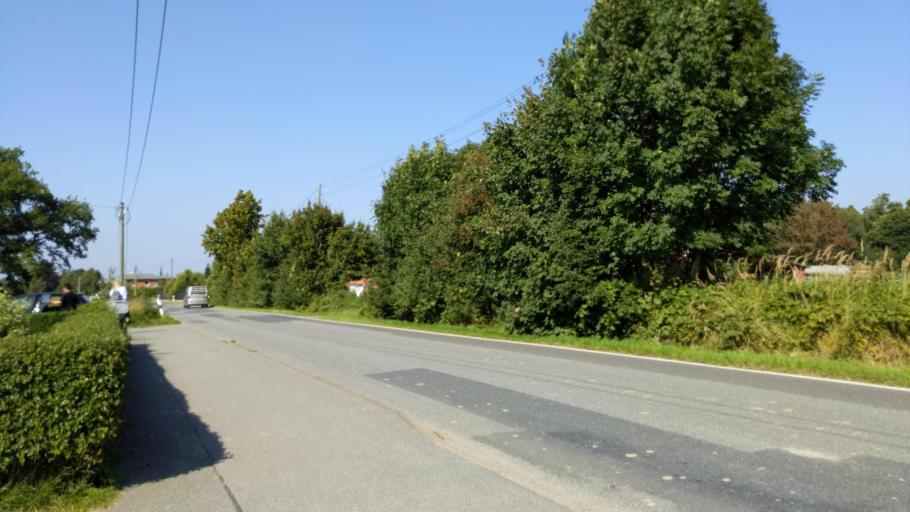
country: DE
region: Schleswig-Holstein
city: Klein Wesenberg
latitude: 53.8077
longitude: 10.5482
